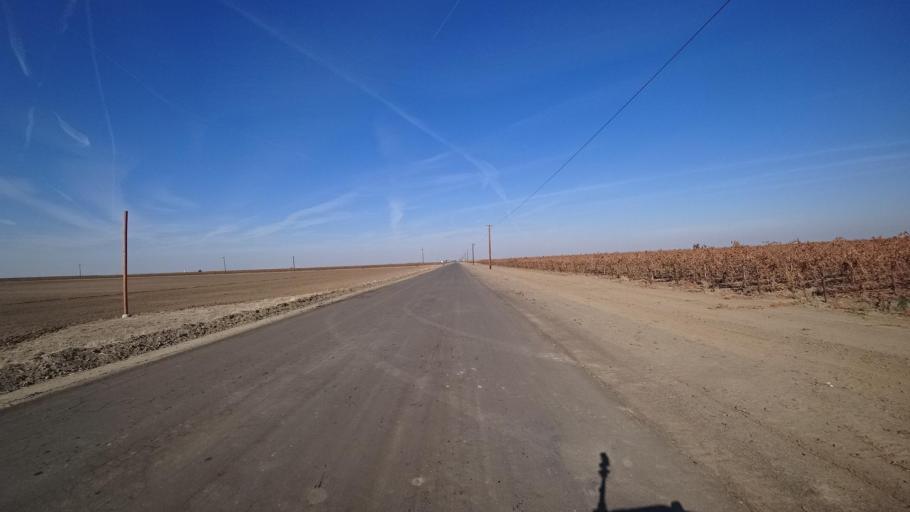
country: US
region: California
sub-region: Kern County
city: Wasco
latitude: 35.6866
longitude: -119.3839
